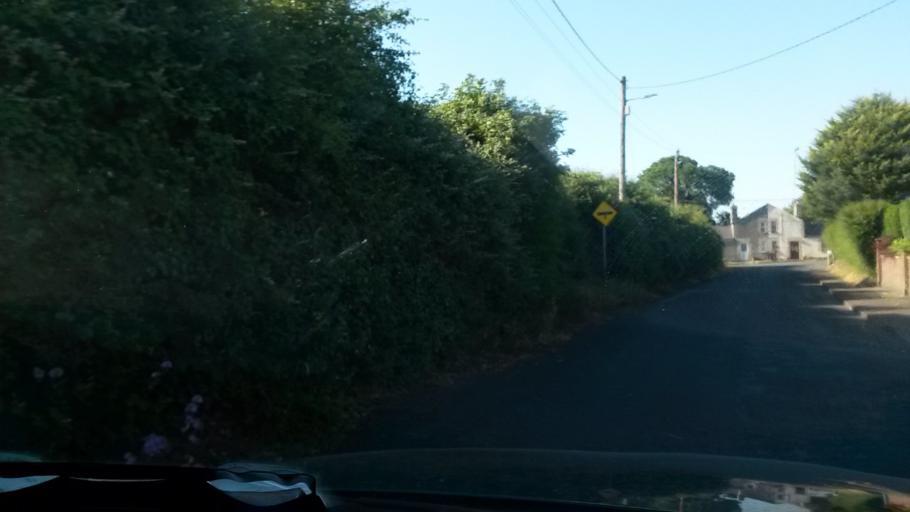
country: IE
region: Leinster
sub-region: Dublin City
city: Finglas
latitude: 53.4258
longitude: -6.3155
